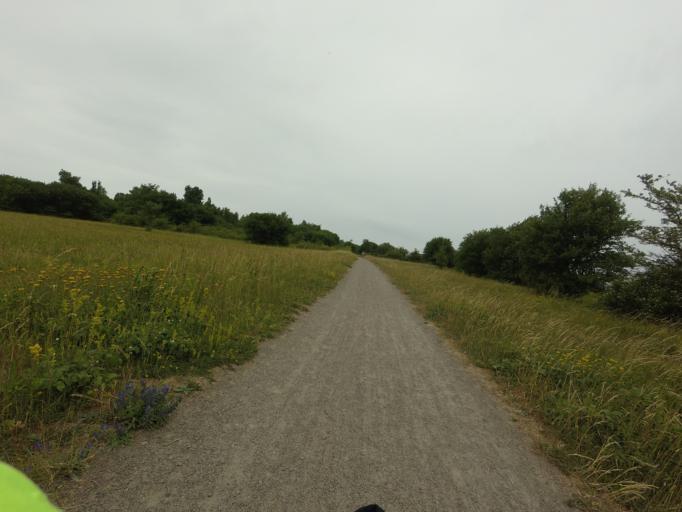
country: SE
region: Skane
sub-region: Malmo
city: Bunkeflostrand
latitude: 55.5262
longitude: 12.9142
